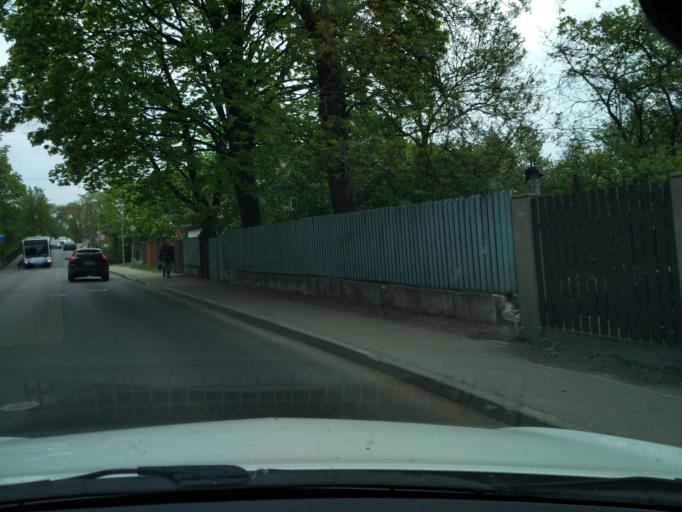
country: LV
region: Riga
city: Riga
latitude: 56.9258
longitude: 24.0822
